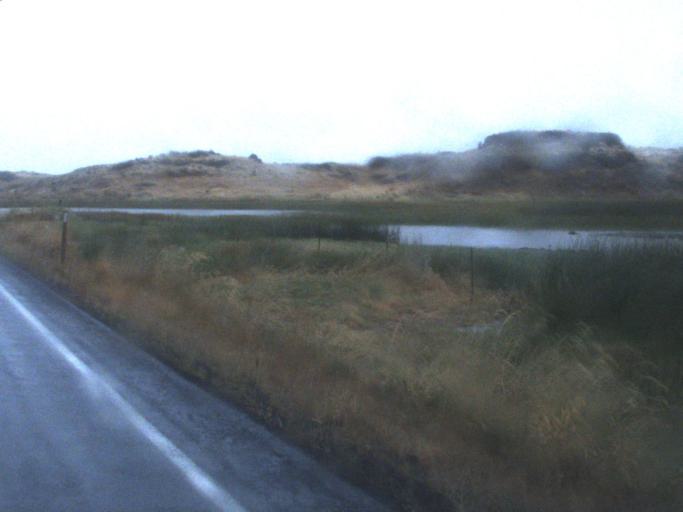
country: US
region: Washington
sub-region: Spokane County
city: Medical Lake
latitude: 47.2706
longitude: -117.9450
